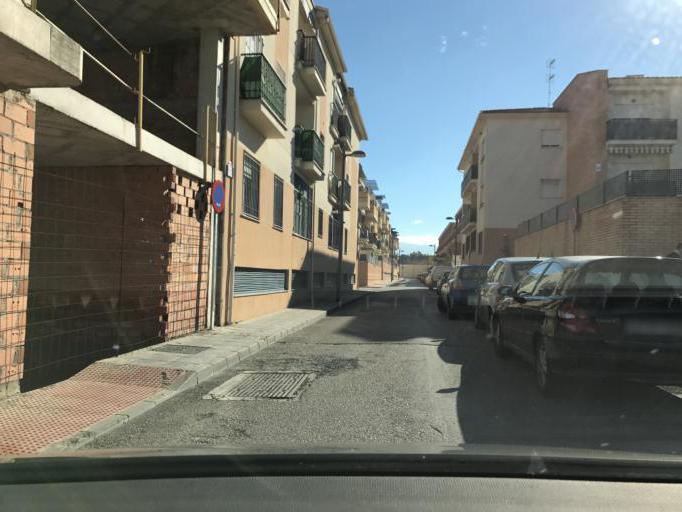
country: ES
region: Andalusia
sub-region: Provincia de Granada
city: Cullar-Vega
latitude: 37.1393
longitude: -3.6660
